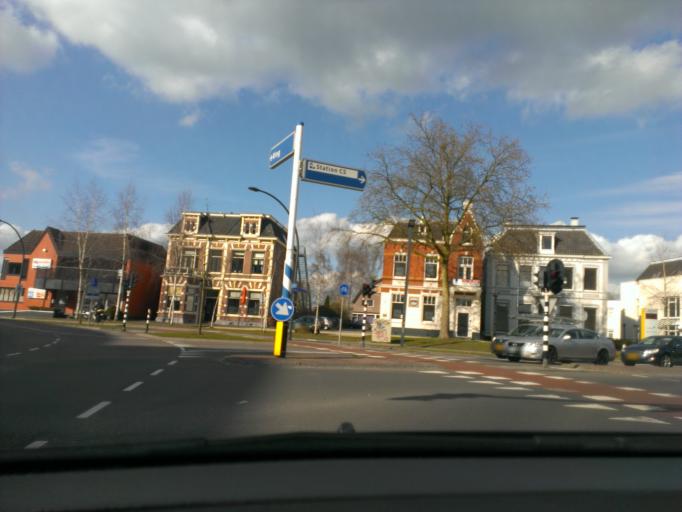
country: NL
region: Overijssel
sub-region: Gemeente Enschede
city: Enschede
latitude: 52.2232
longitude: 6.8875
